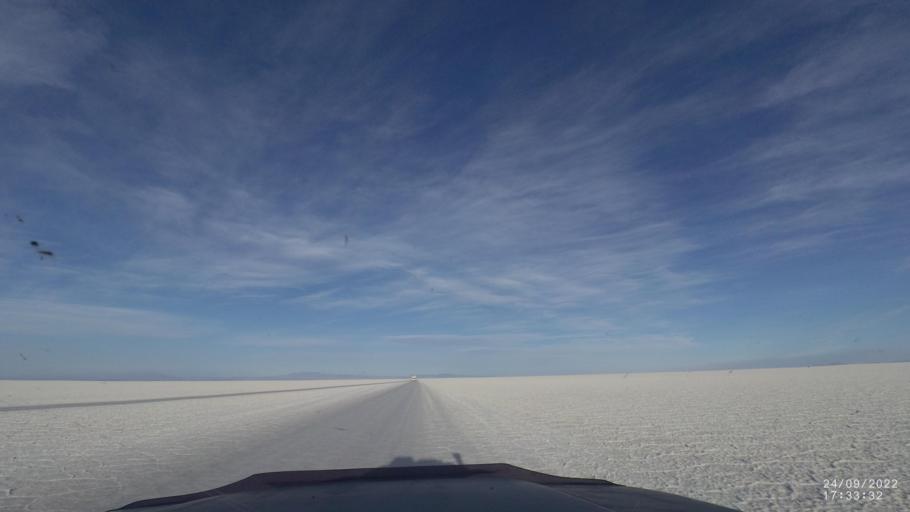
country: BO
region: Potosi
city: Colchani
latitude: -20.3199
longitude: -67.3034
